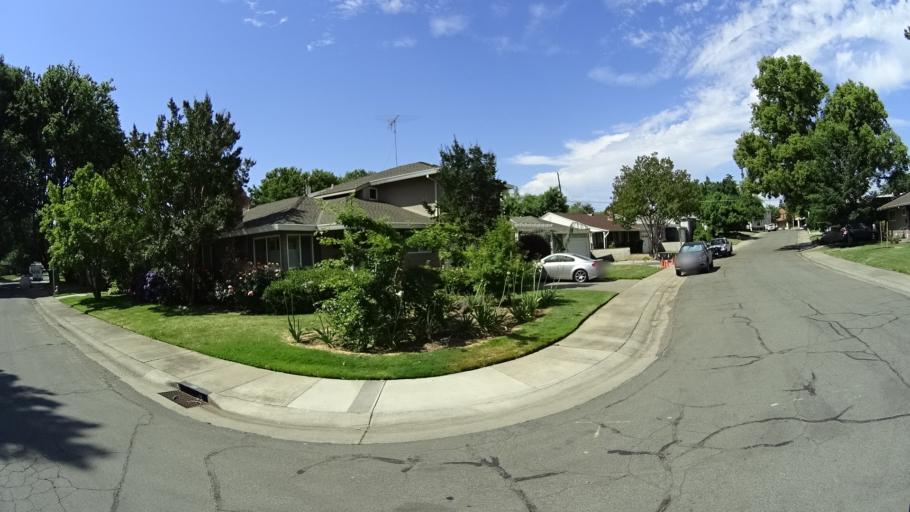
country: US
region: California
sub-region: Sacramento County
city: Arden-Arcade
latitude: 38.5733
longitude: -121.4305
